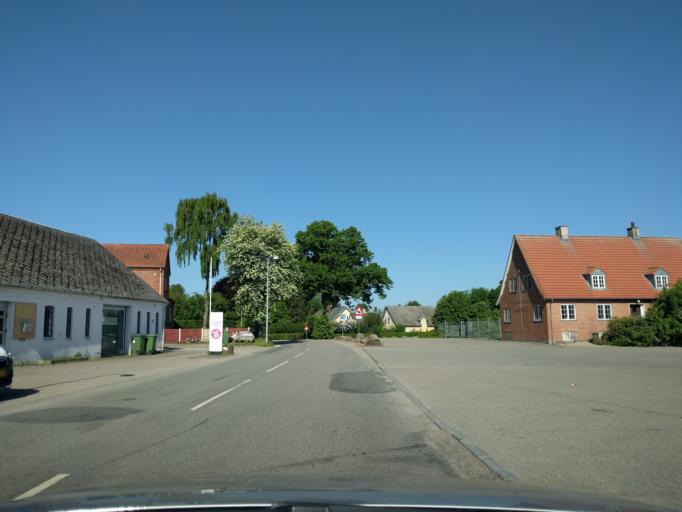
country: DK
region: South Denmark
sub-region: Odense Kommune
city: Bellinge
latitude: 55.3573
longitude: 10.3265
